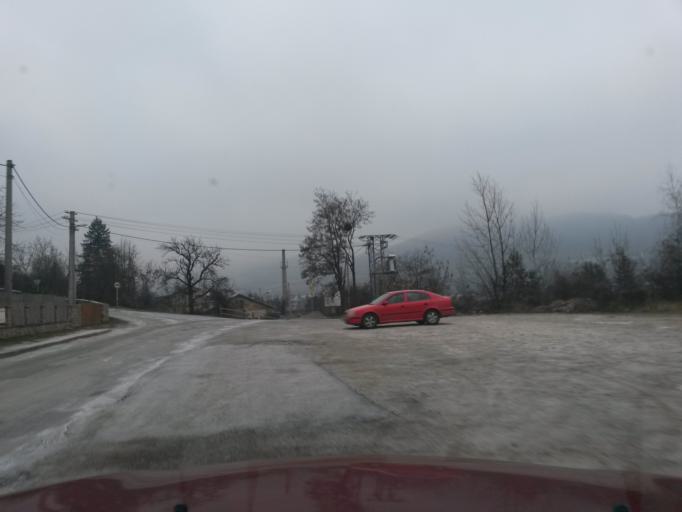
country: SK
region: Kosicky
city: Roznava
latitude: 48.6652
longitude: 20.5137
